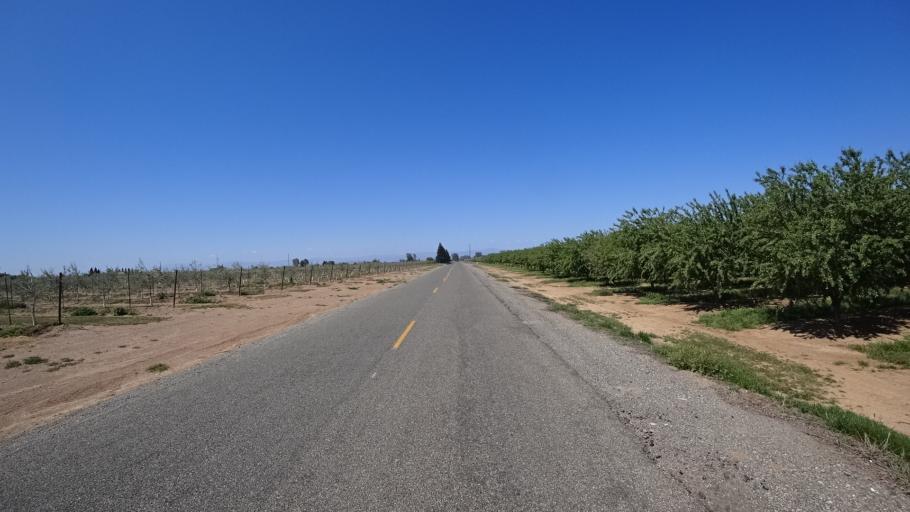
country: US
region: California
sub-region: Glenn County
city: Orland
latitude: 39.7870
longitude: -122.1666
